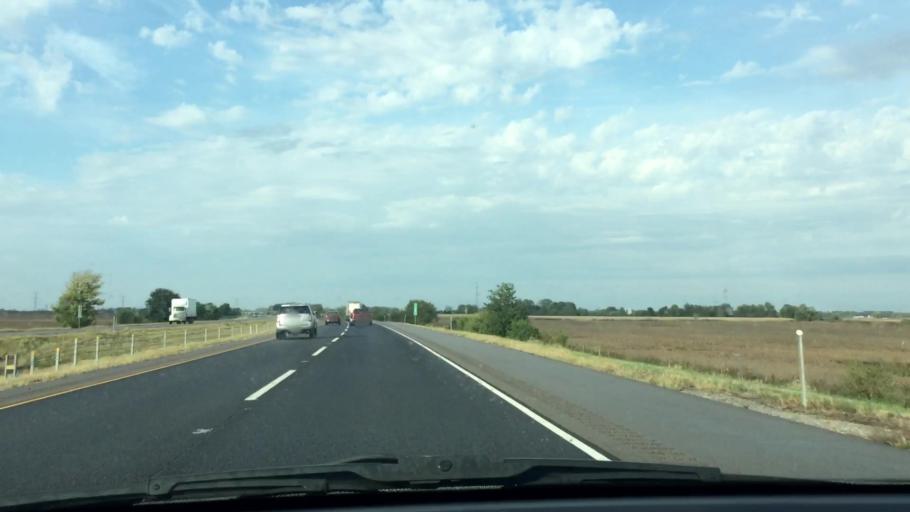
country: US
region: Illinois
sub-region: Lee County
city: Dixon
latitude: 41.7788
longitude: -89.5647
